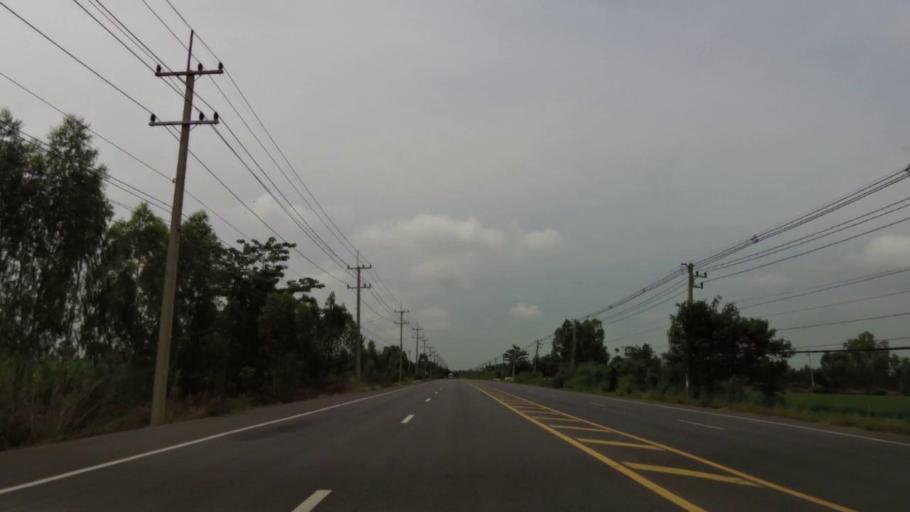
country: TH
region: Lop Buri
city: Khok Samrong
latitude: 15.0651
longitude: 100.6357
